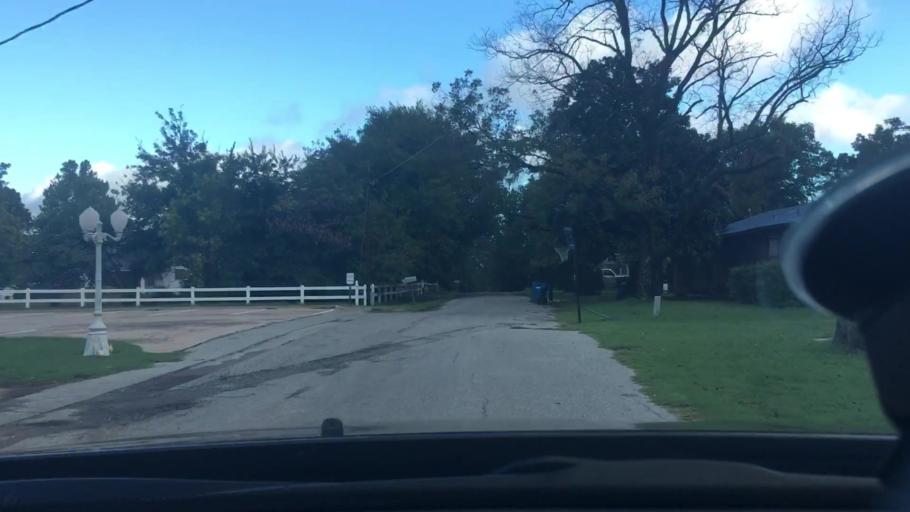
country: US
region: Oklahoma
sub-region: Coal County
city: Coalgate
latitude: 34.5414
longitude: -96.2219
